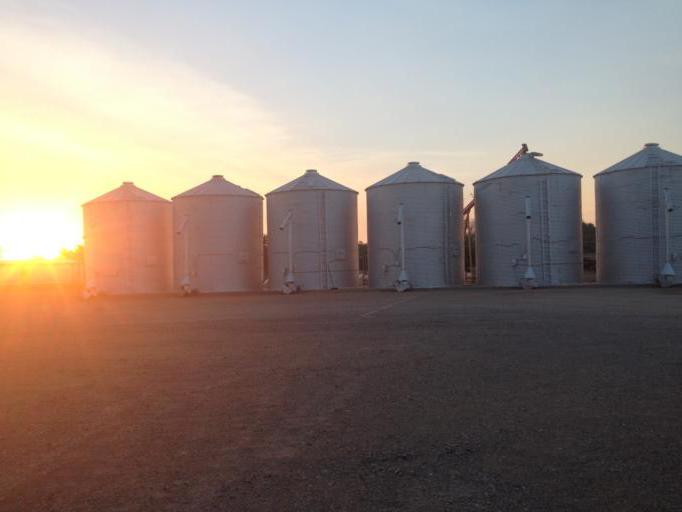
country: US
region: Texas
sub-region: Hardeman County
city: Quanah
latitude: 34.2582
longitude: -99.5113
